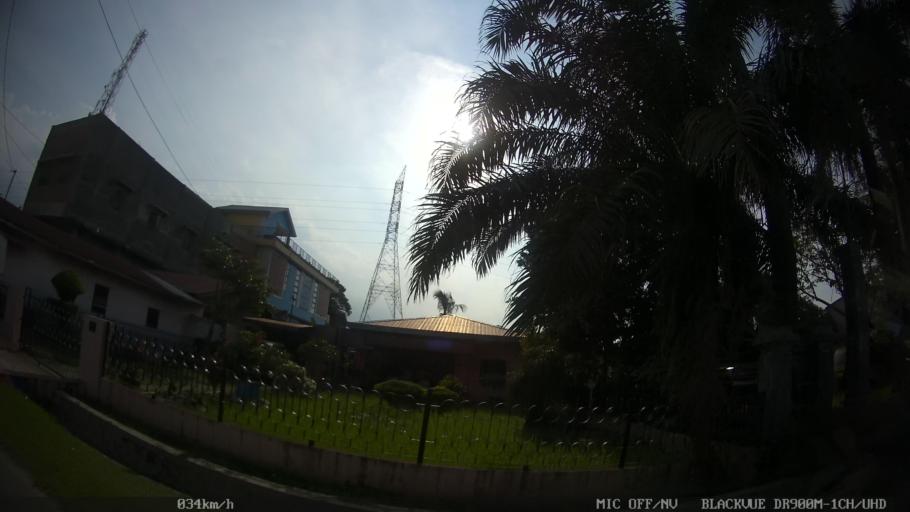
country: ID
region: North Sumatra
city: Binjai
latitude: 3.6043
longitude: 98.5113
